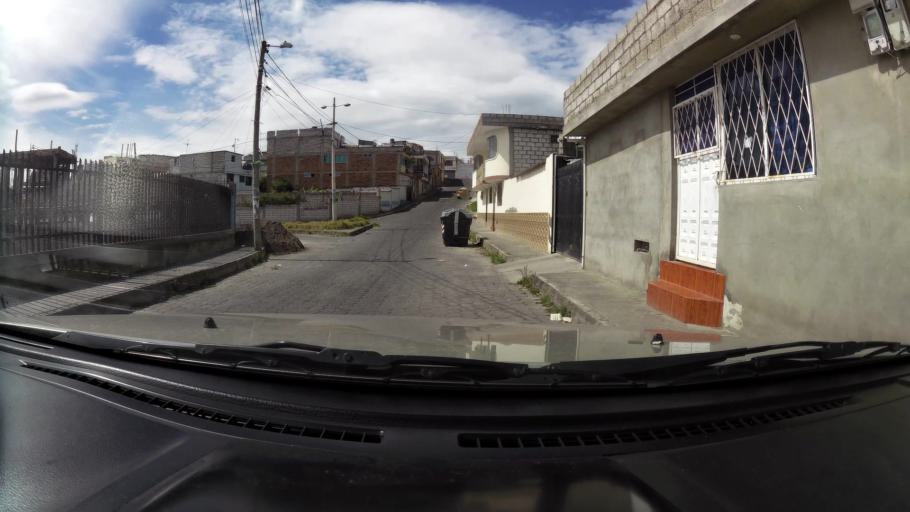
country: EC
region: Cotopaxi
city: Latacunga
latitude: -0.9343
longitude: -78.6063
